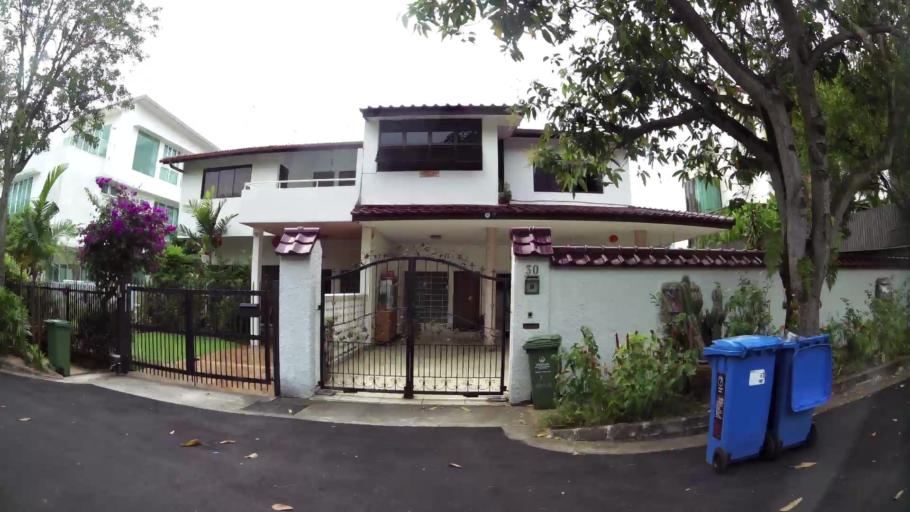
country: SG
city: Singapore
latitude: 1.3135
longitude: 103.7829
